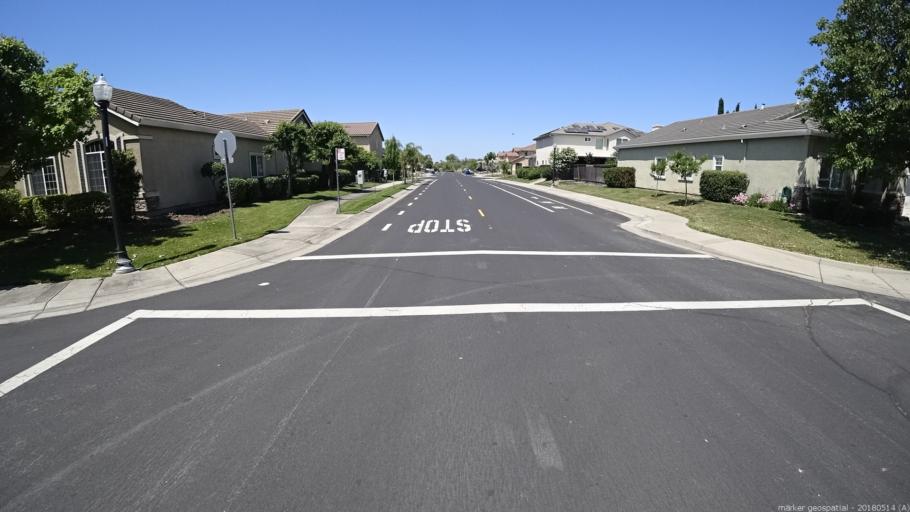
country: US
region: California
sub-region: Yolo County
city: West Sacramento
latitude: 38.6306
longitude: -121.5302
